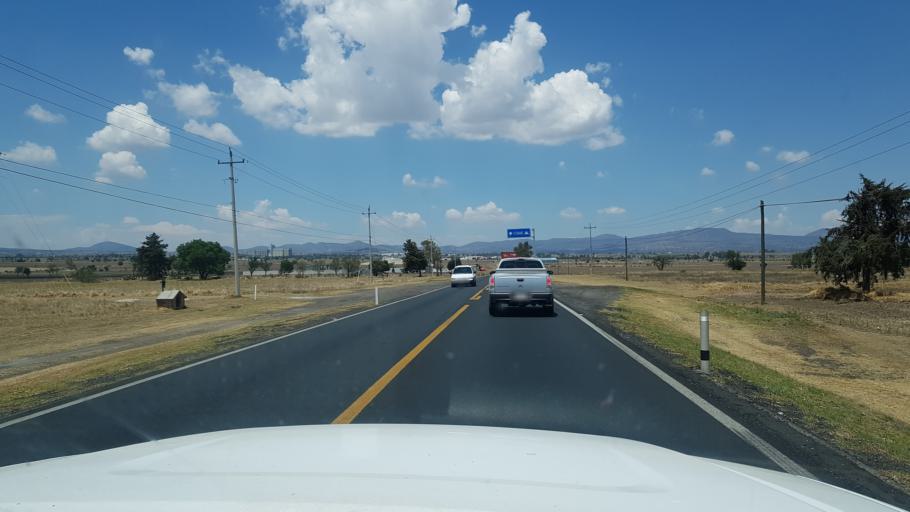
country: MX
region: Hidalgo
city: Calpulalpan
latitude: 19.5759
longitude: -98.5157
